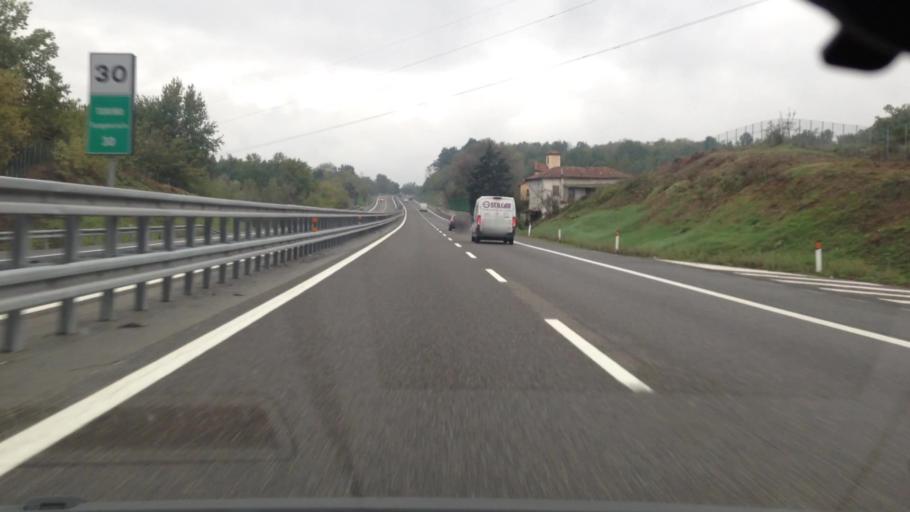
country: IT
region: Piedmont
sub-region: Provincia di Asti
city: Revigliasco d'Asti
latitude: 44.9029
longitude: 8.1444
